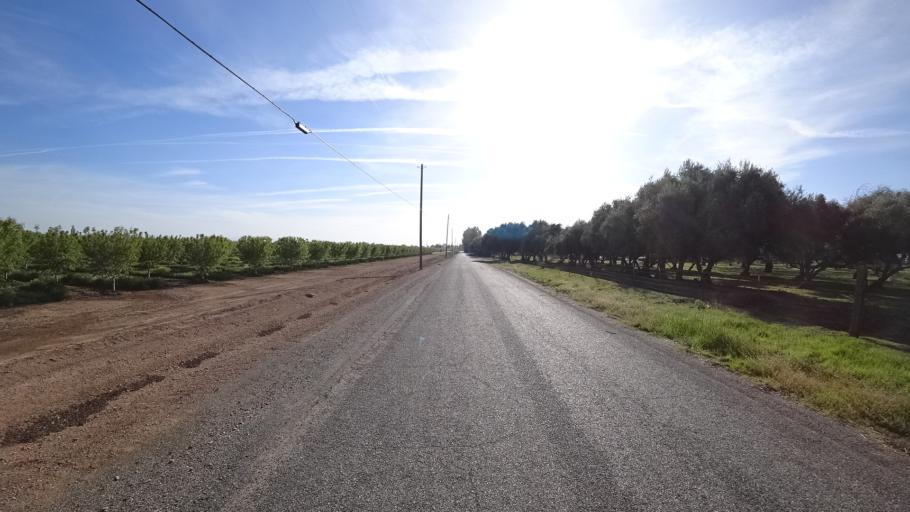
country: US
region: California
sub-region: Glenn County
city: Orland
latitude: 39.7188
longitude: -122.2315
